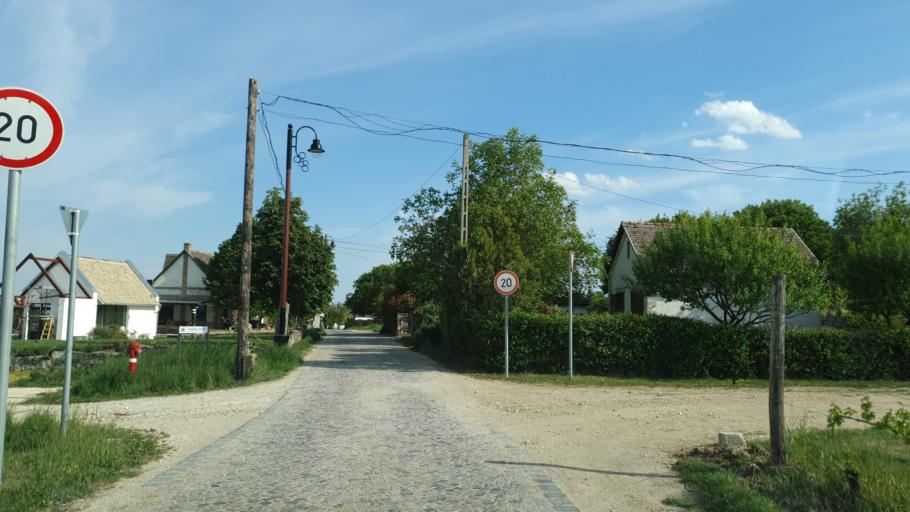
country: HU
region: Fejer
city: Etyek
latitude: 47.4418
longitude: 18.7382
